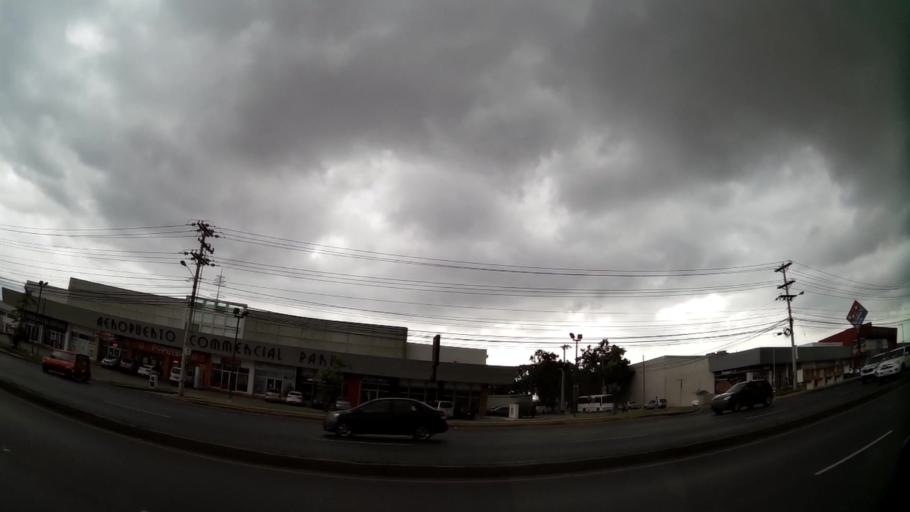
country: PA
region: Panama
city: Tocumen
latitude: 9.0630
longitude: -79.4204
